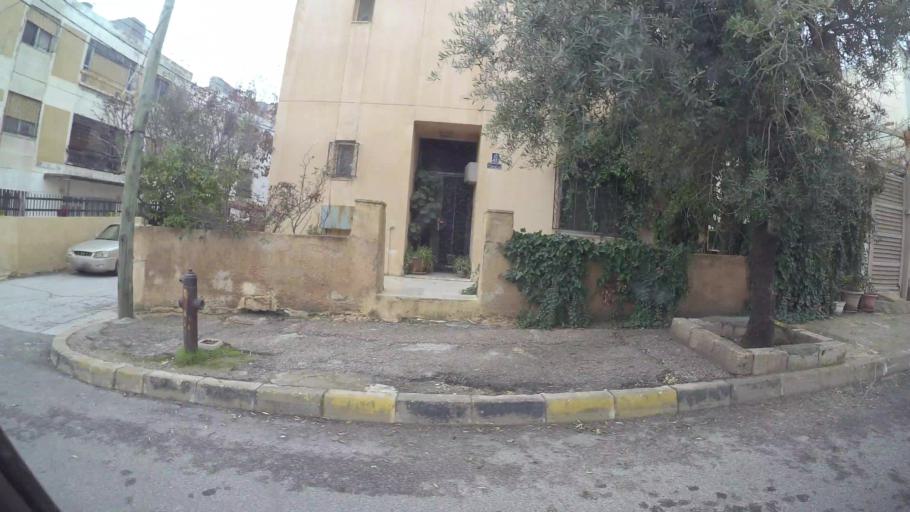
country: JO
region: Amman
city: Al Jubayhah
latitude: 32.0541
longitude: 35.8812
